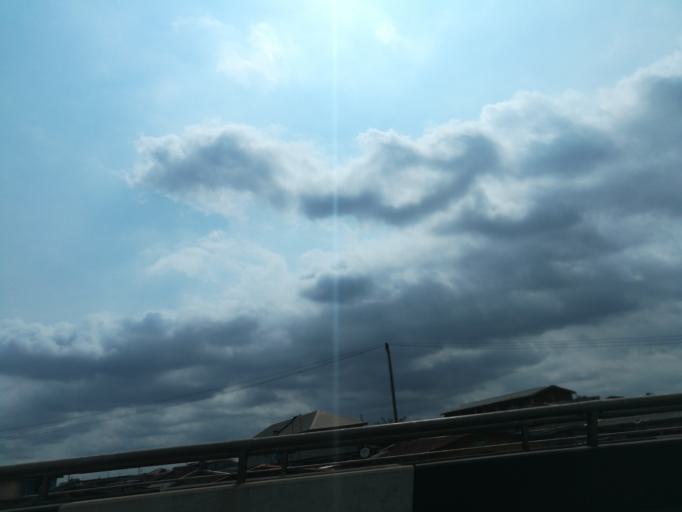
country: NG
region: Lagos
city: Somolu
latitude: 6.5376
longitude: 3.4002
